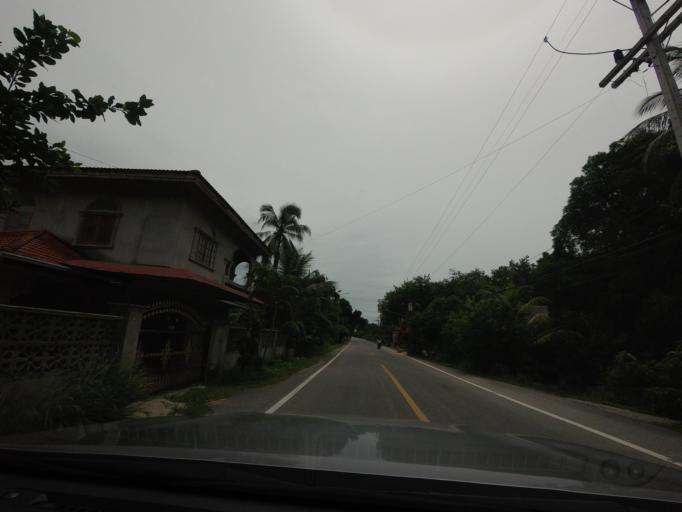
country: TH
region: Pattani
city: Kapho
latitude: 6.6093
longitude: 101.5391
